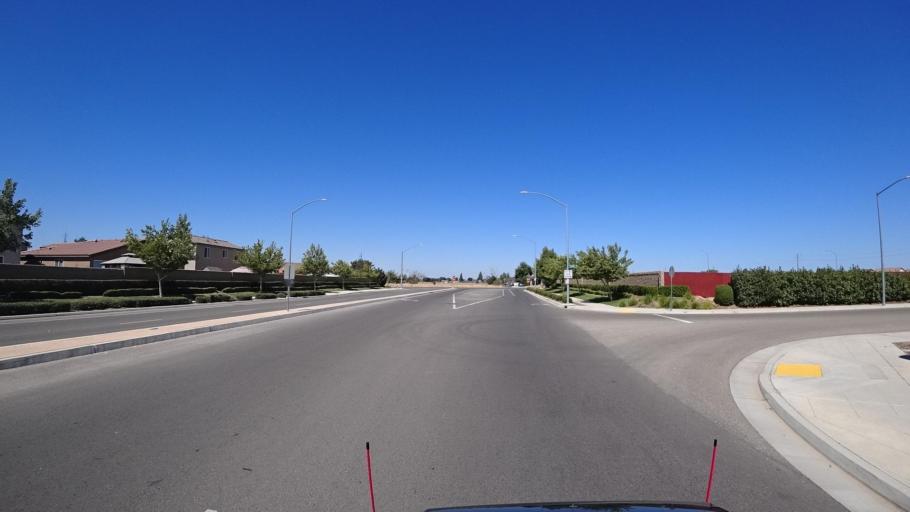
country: US
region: California
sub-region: Fresno County
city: Sunnyside
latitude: 36.7206
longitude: -119.6719
